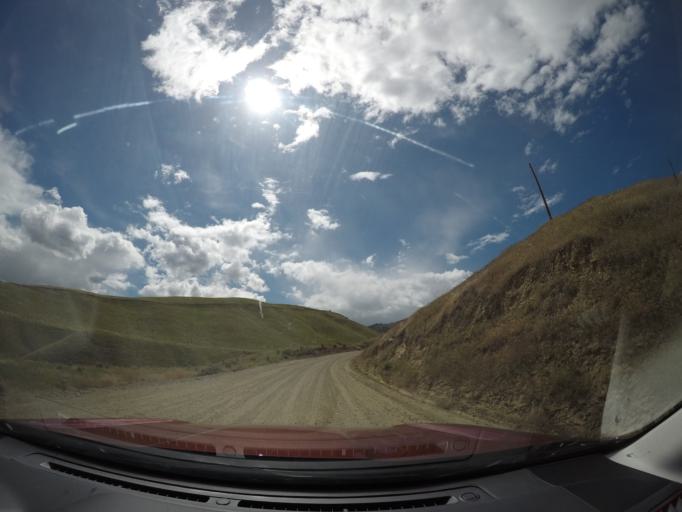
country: US
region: Washington
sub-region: Chelan County
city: West Wenatchee
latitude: 47.4604
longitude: -120.3571
